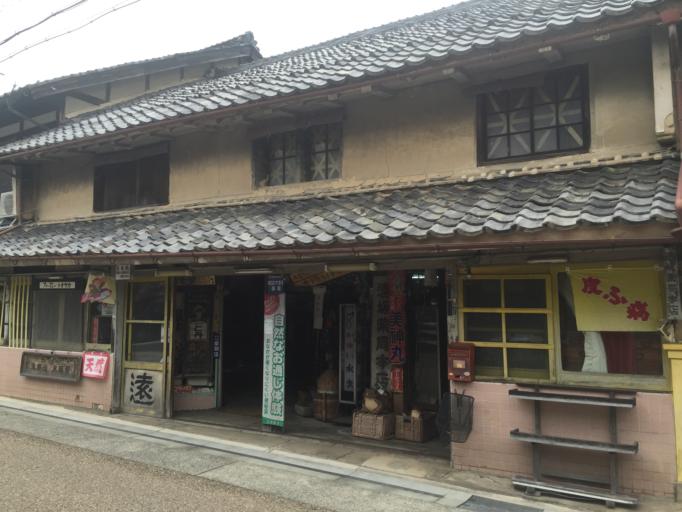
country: JP
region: Kyoto
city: Ayabe
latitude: 35.2975
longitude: 135.2600
